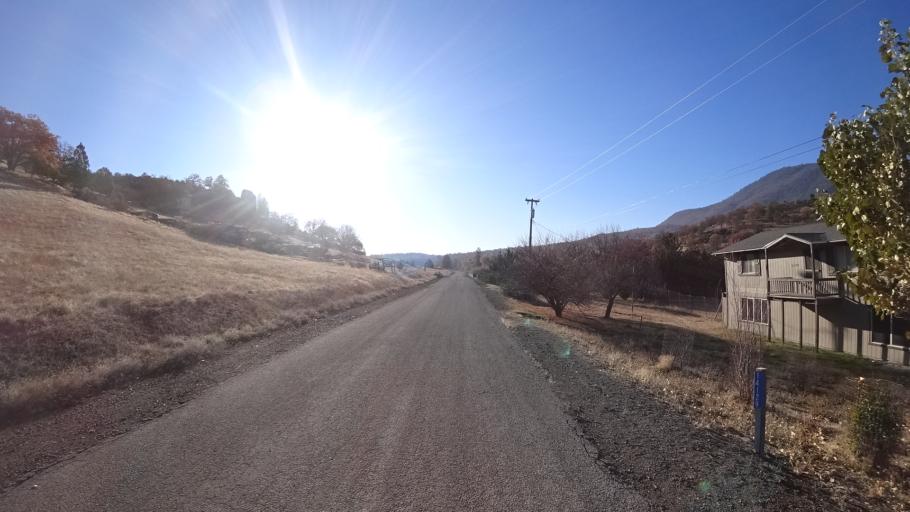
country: US
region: California
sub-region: Siskiyou County
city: Montague
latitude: 41.8942
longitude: -122.4939
